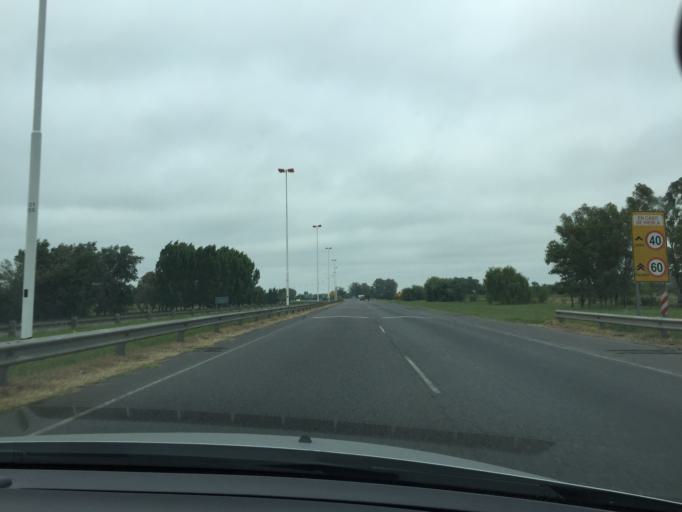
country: AR
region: Buenos Aires
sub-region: Partido de Ezeiza
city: Ezeiza
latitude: -34.8629
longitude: -58.5692
